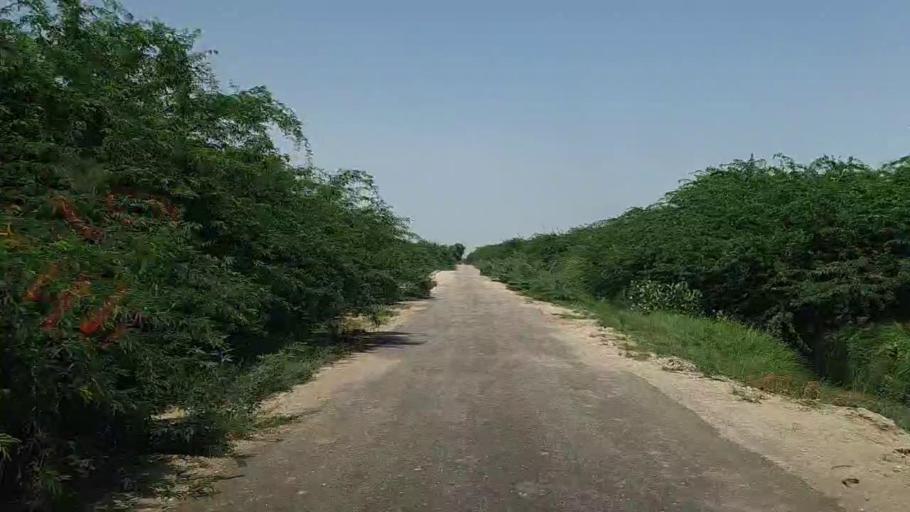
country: PK
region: Sindh
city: Pad Idan
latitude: 26.7395
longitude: 68.3129
